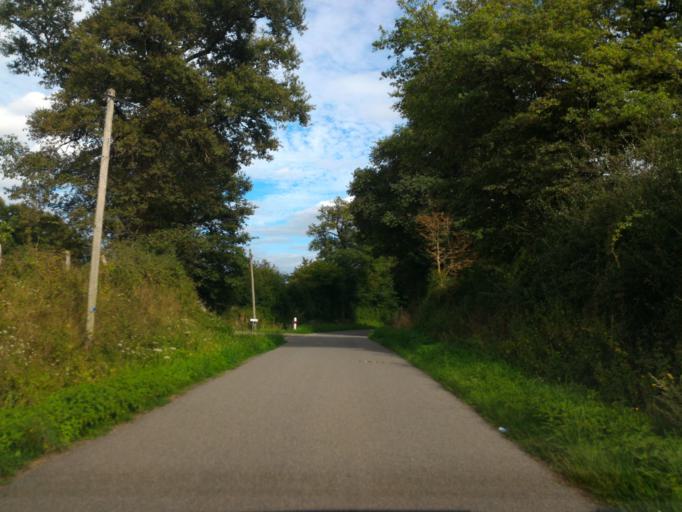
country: FR
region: Poitou-Charentes
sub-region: Departement de la Charente
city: Etagnac
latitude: 45.9442
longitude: 0.7957
